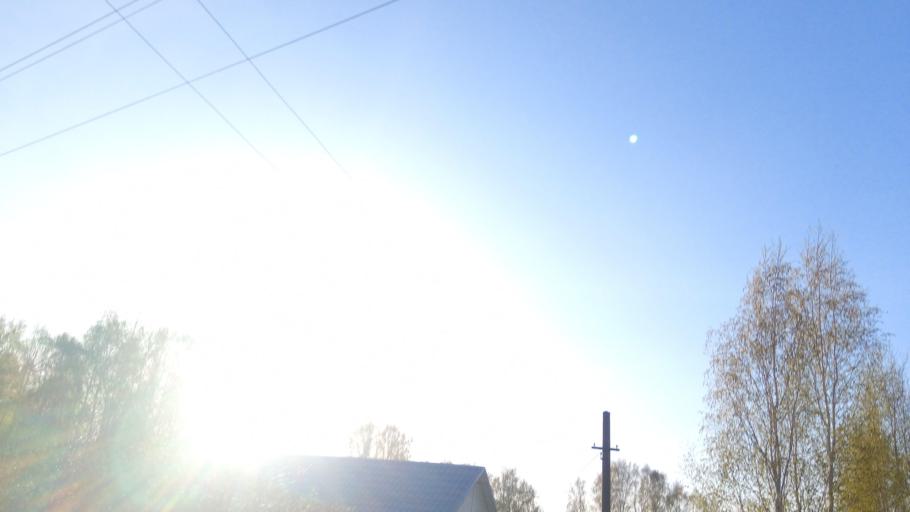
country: RU
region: Chelyabinsk
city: Timiryazevskiy
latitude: 54.9941
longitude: 60.8442
